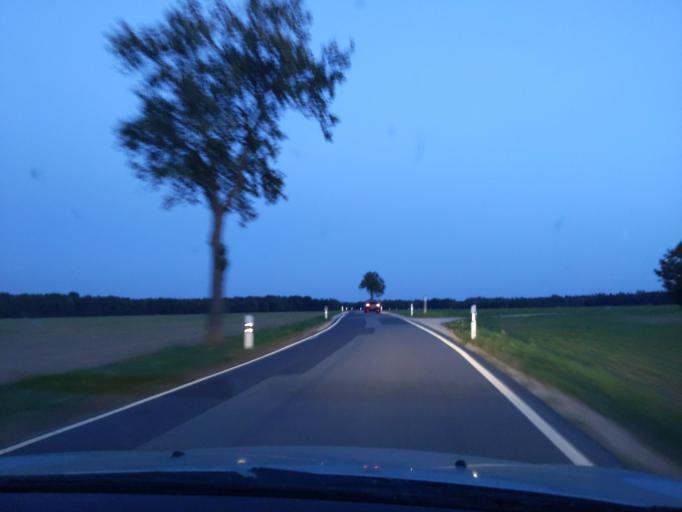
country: DE
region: Saxony
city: Grossdubrau
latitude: 51.2947
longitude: 14.4646
